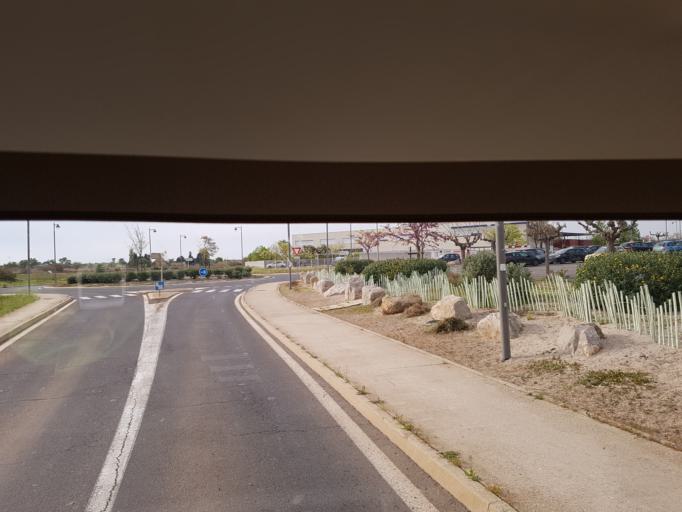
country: FR
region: Languedoc-Roussillon
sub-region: Departement de l'Herault
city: Marseillan
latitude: 43.3622
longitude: 3.5220
